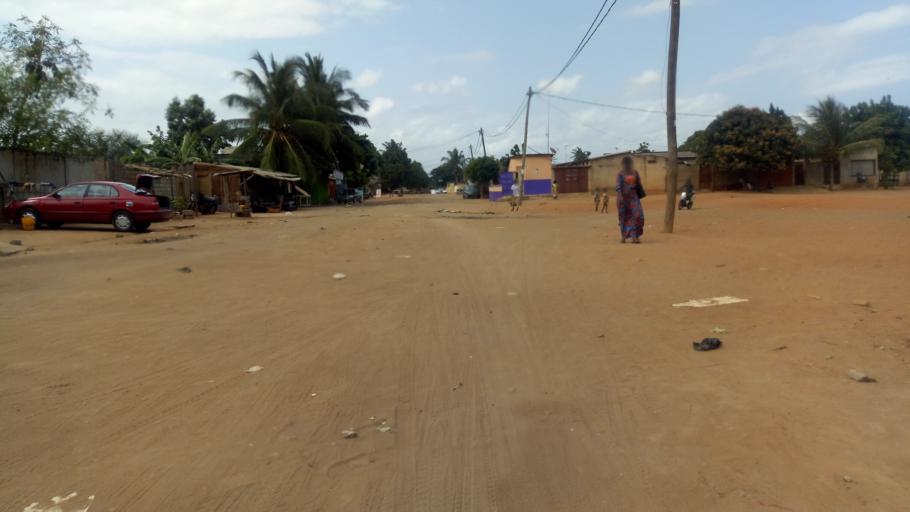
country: TG
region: Maritime
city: Lome
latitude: 6.2259
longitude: 1.1794
